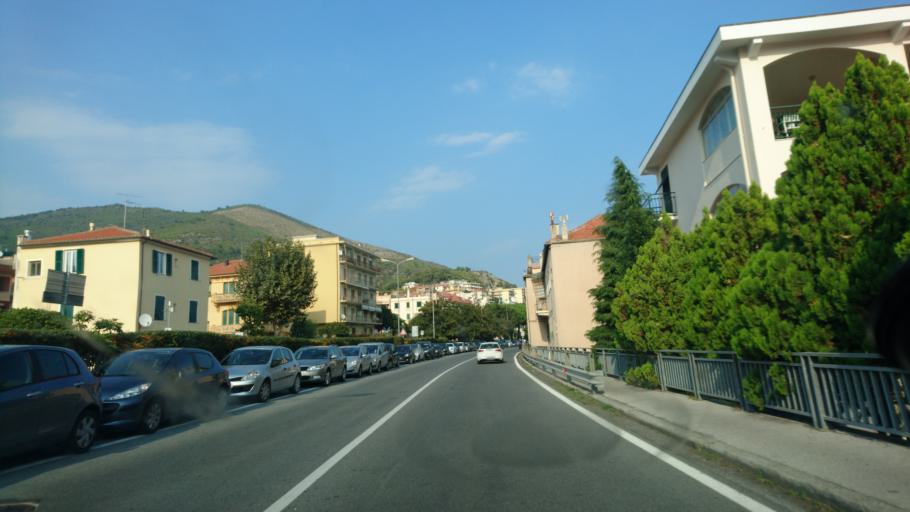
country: IT
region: Liguria
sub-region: Provincia di Savona
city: Spotorno
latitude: 44.2271
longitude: 8.4167
